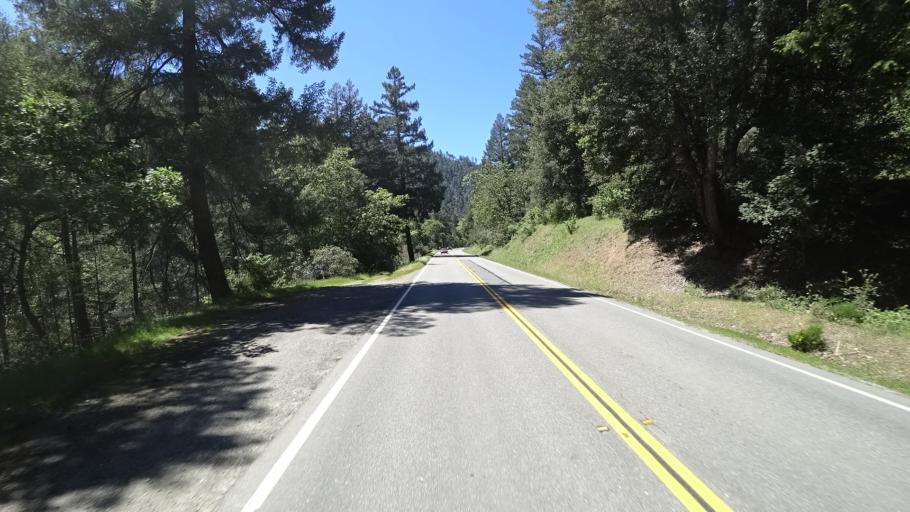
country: US
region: California
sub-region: Trinity County
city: Hayfork
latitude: 40.7502
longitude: -123.2770
